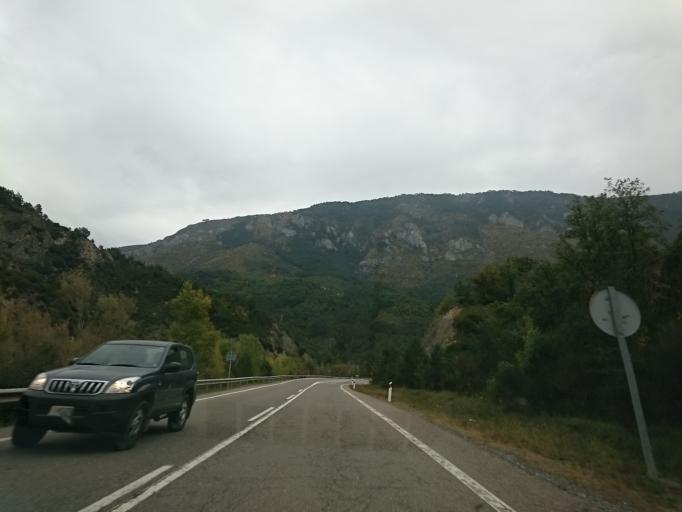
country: ES
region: Catalonia
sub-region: Provincia de Lleida
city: Sort
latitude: 42.3128
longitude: 1.0603
